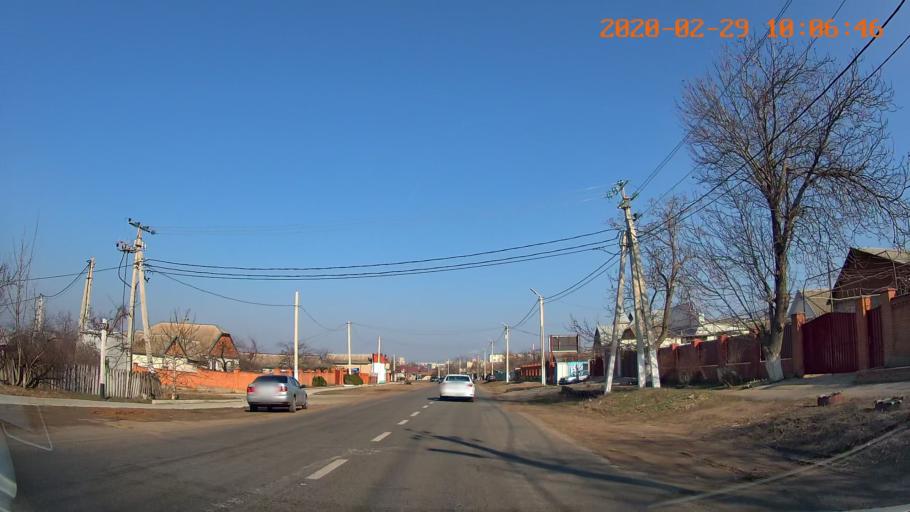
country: MD
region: Telenesti
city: Tiraspolul Nou
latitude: 46.8172
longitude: 29.6686
